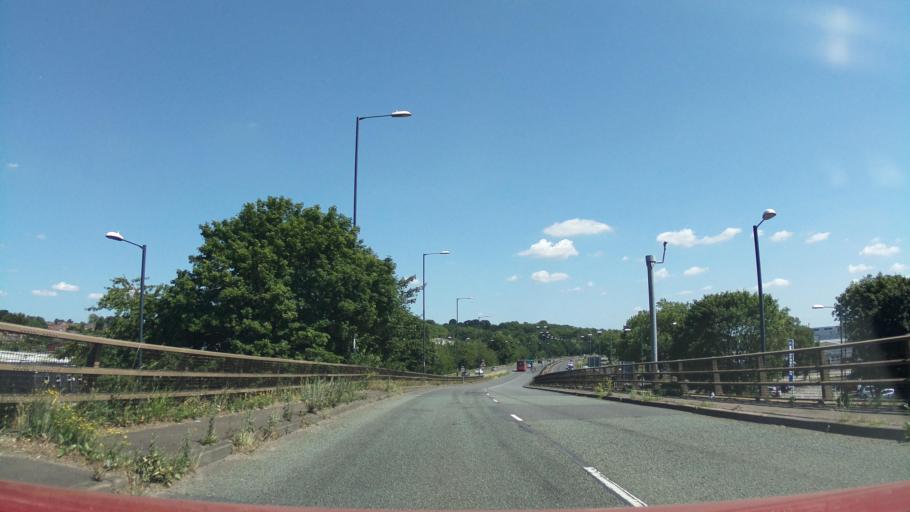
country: GB
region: England
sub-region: Derby
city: Derby
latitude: 52.9246
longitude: -1.4610
